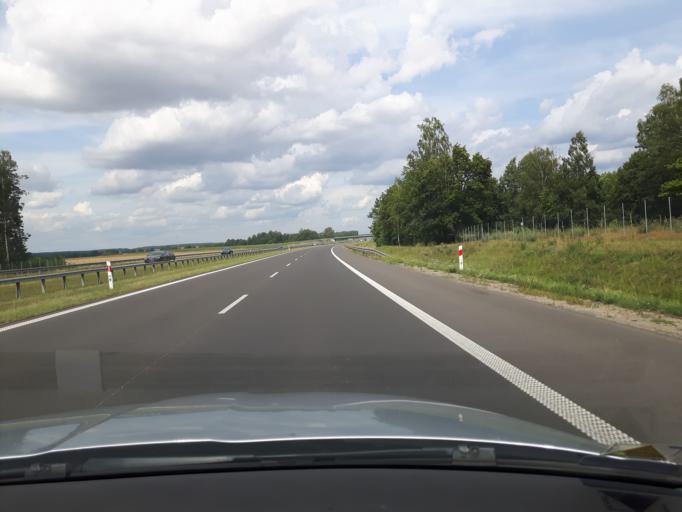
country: PL
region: Masovian Voivodeship
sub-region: Powiat mlawski
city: Wieczfnia Koscielna
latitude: 53.2571
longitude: 20.4255
